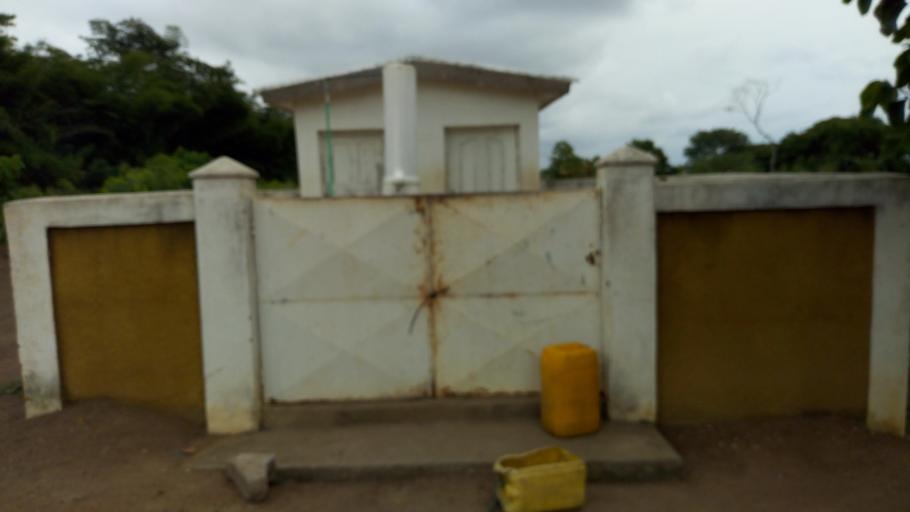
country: CI
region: Vallee du Bandama
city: Bouake
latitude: 7.6797
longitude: -5.0997
